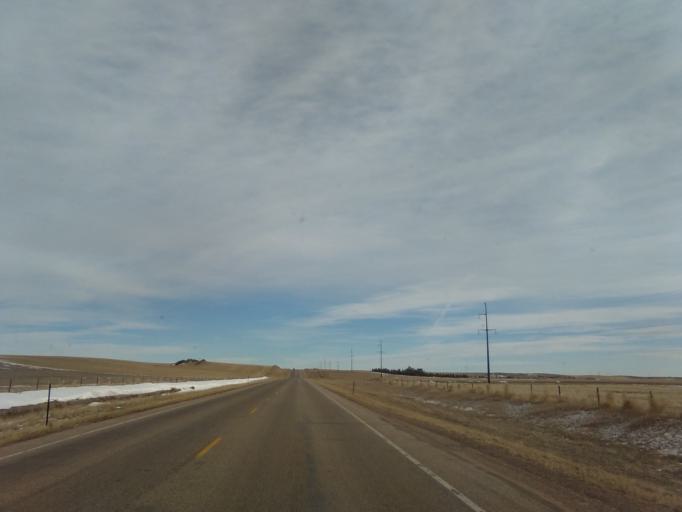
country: US
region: Wyoming
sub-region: Laramie County
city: Ranchettes
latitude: 41.3770
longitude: -104.5391
